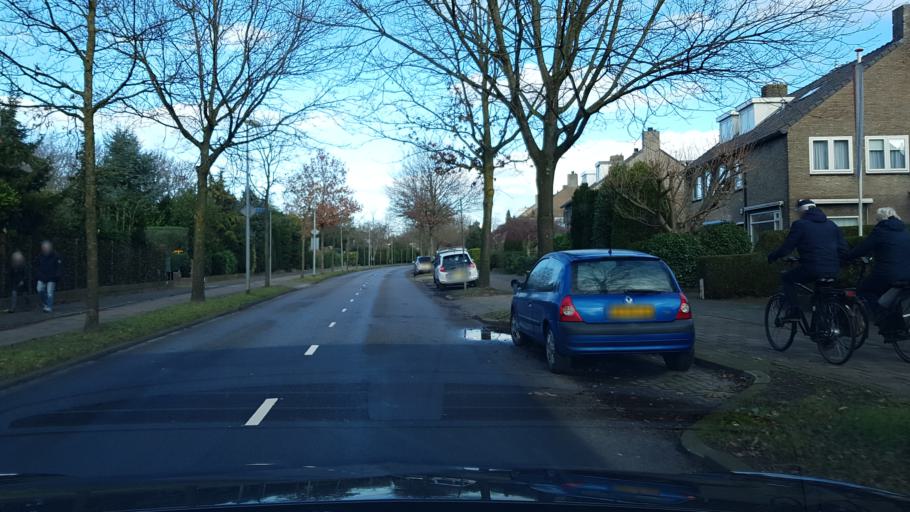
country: NL
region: North Holland
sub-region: Gemeente Bussum
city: Bussum
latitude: 52.2814
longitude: 5.1474
